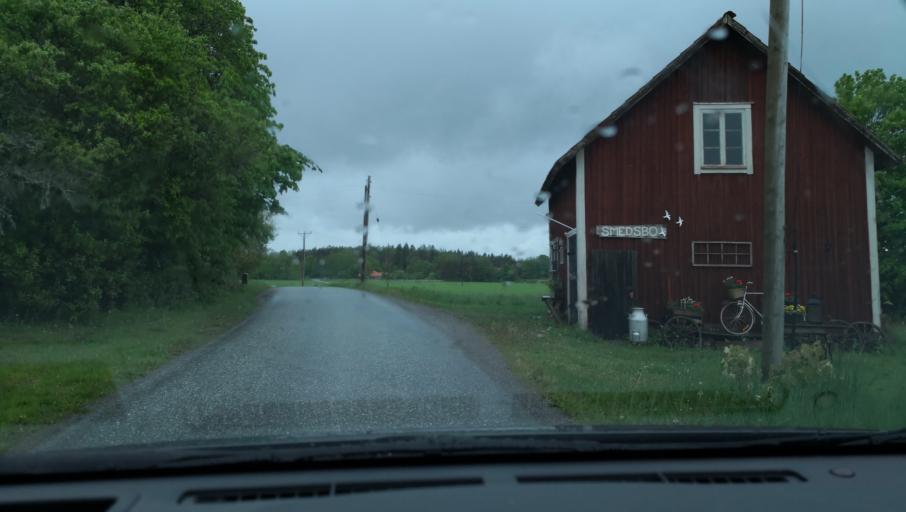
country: SE
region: Uppsala
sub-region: Enkopings Kommun
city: Orsundsbro
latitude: 59.7660
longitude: 17.3419
